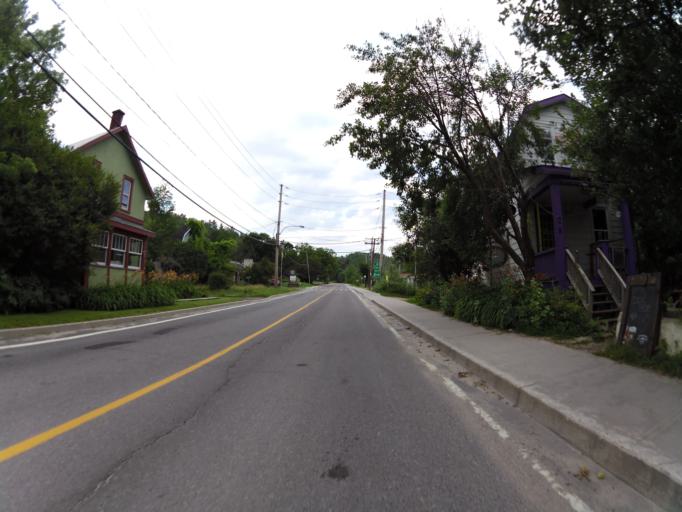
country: CA
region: Quebec
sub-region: Outaouais
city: Wakefield
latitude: 45.6325
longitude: -75.9293
